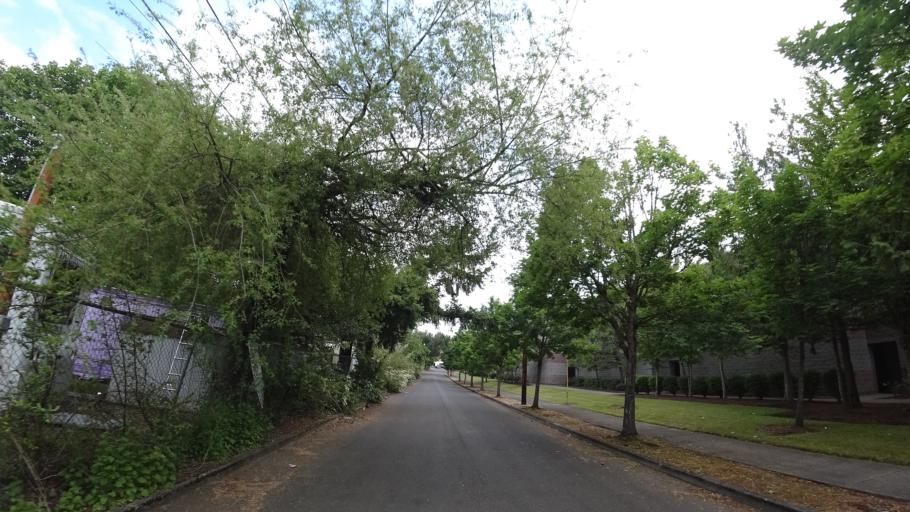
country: US
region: Oregon
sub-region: Multnomah County
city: Gresham
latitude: 45.5062
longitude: -122.4915
